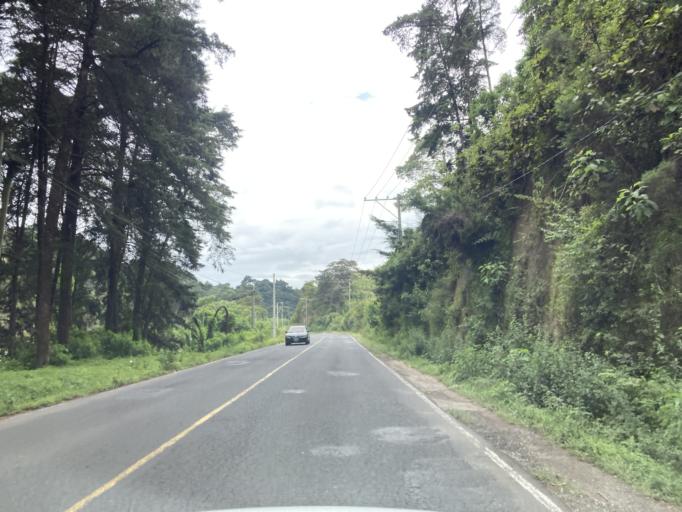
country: GT
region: Guatemala
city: San Jose Pinula
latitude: 14.5330
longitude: -90.4096
